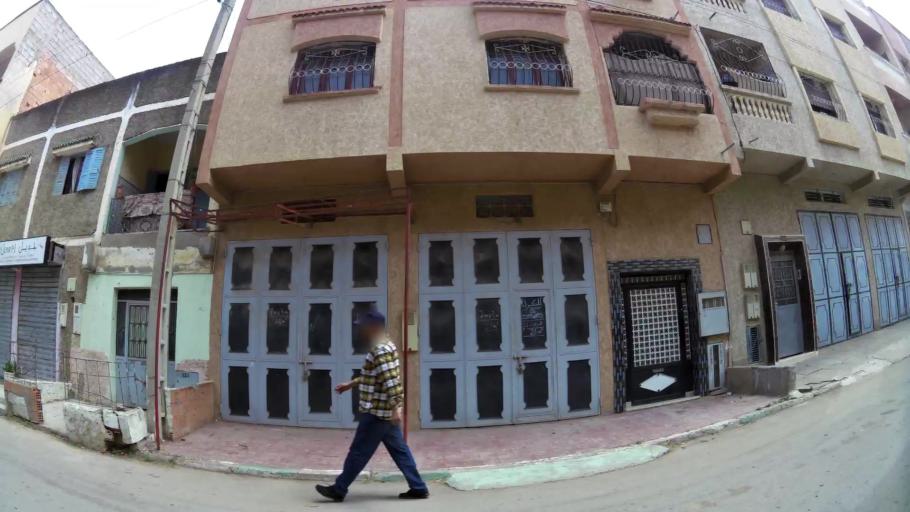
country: MA
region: Rabat-Sale-Zemmour-Zaer
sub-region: Khemisset
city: Tiflet
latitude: 34.0091
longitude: -6.5316
